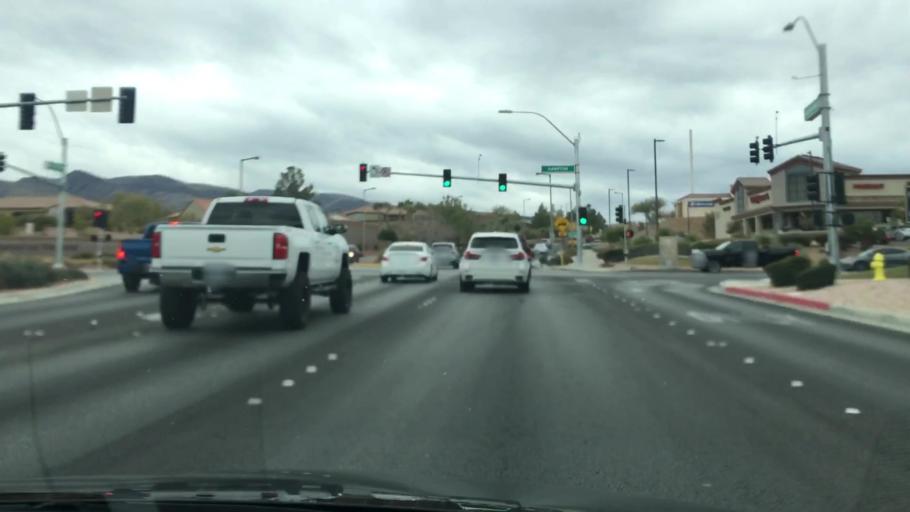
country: US
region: Nevada
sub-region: Clark County
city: Whitney
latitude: 35.9548
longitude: -115.0936
